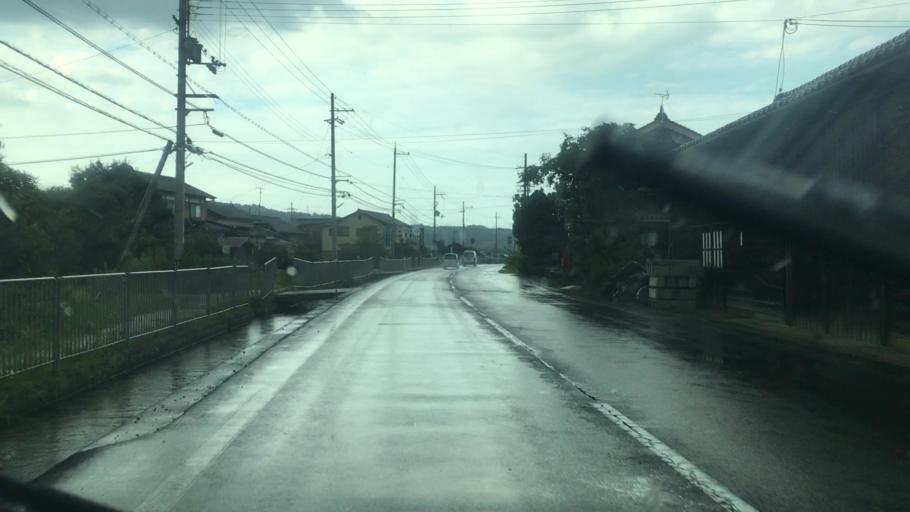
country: JP
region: Hyogo
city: Toyooka
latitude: 35.4906
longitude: 134.8159
